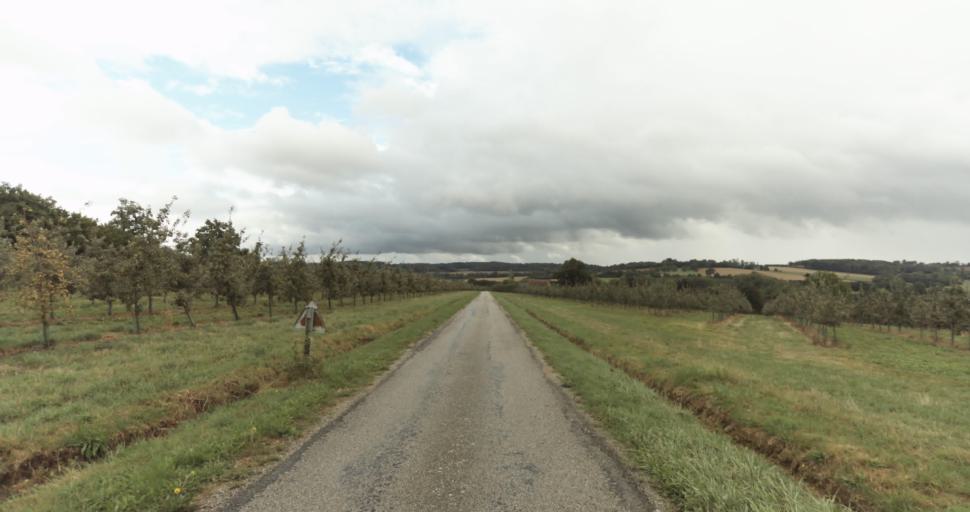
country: FR
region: Lower Normandy
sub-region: Departement de l'Orne
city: Sainte-Gauburge-Sainte-Colombe
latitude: 48.7175
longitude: 0.3925
